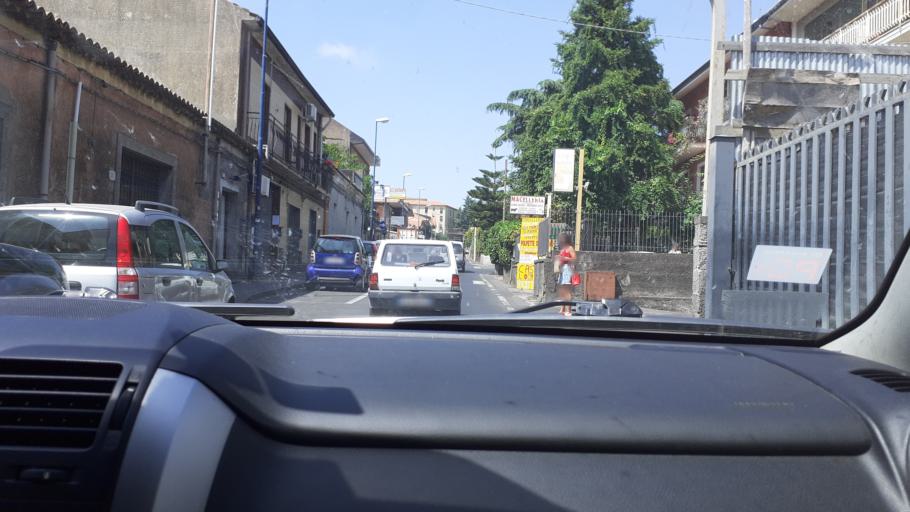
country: IT
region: Sicily
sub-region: Catania
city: Pedara
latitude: 37.6163
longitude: 15.0552
